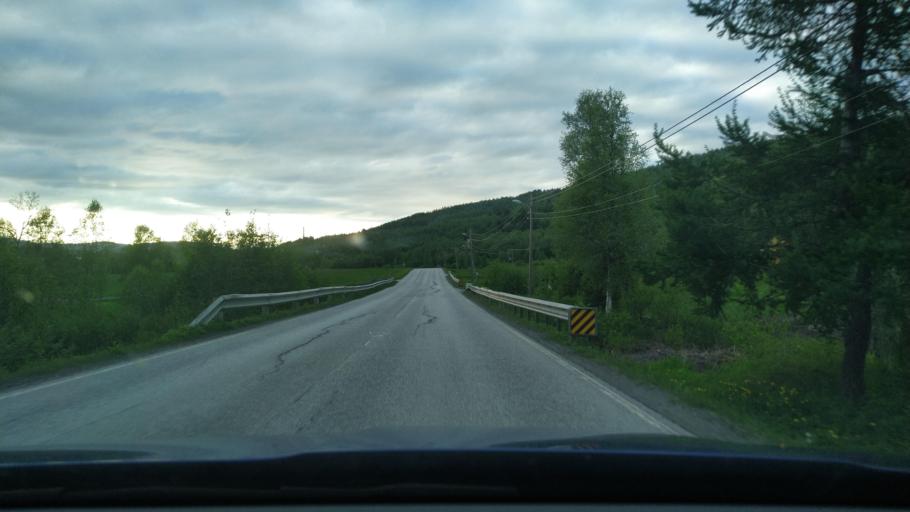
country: NO
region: Troms
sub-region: Sorreisa
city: Sorreisa
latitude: 69.1240
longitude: 18.2171
